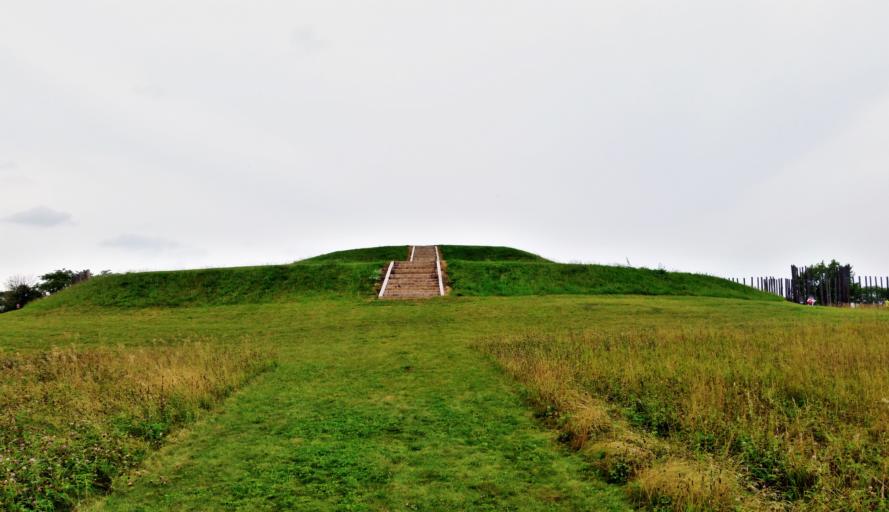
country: US
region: Wisconsin
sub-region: Jefferson County
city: Lake Mills
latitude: 43.0645
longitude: -88.8617
